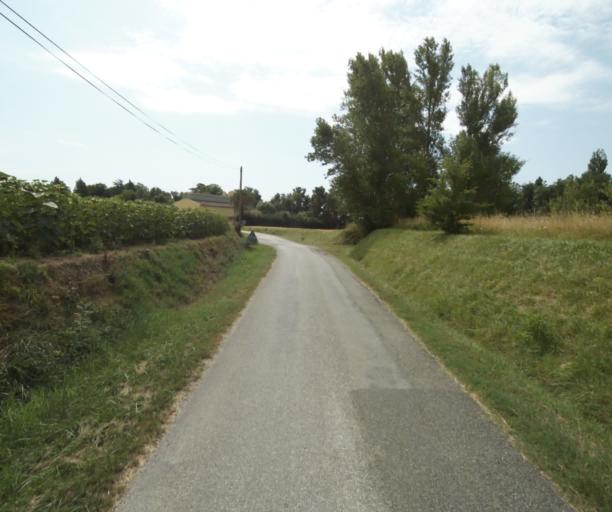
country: FR
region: Midi-Pyrenees
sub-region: Departement de la Haute-Garonne
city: Saint-Felix-Lauragais
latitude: 43.4280
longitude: 1.8988
